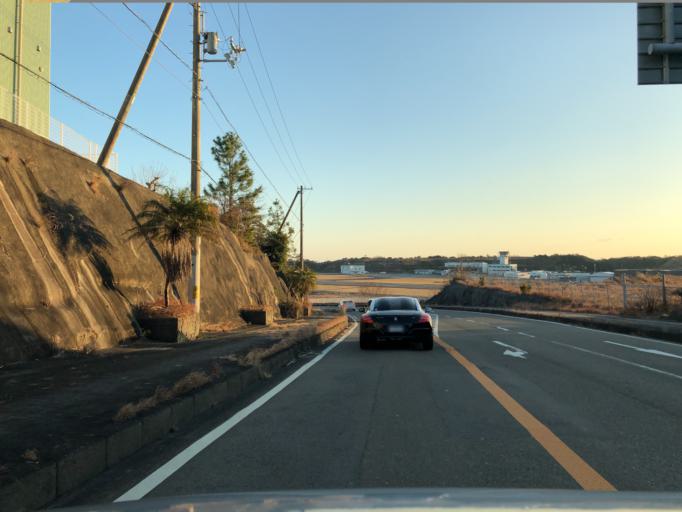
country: JP
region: Wakayama
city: Tanabe
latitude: 33.6688
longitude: 135.3624
